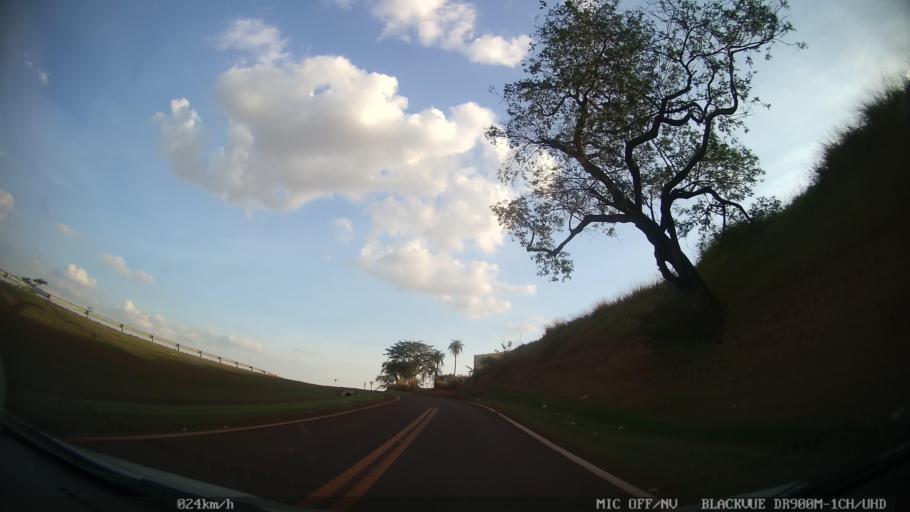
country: BR
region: Sao Paulo
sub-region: Jardinopolis
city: Jardinopolis
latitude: -21.1022
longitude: -47.7668
